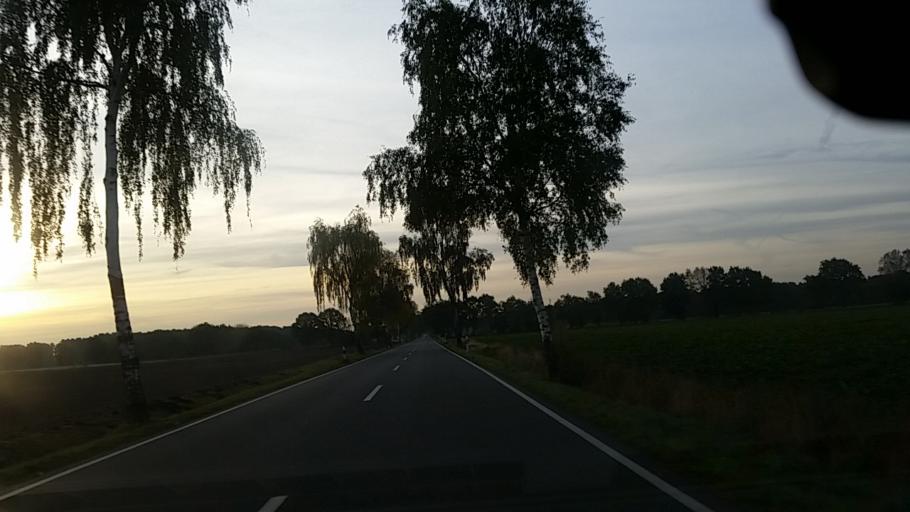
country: DE
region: Lower Saxony
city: Tiddische
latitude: 52.4921
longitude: 10.8039
